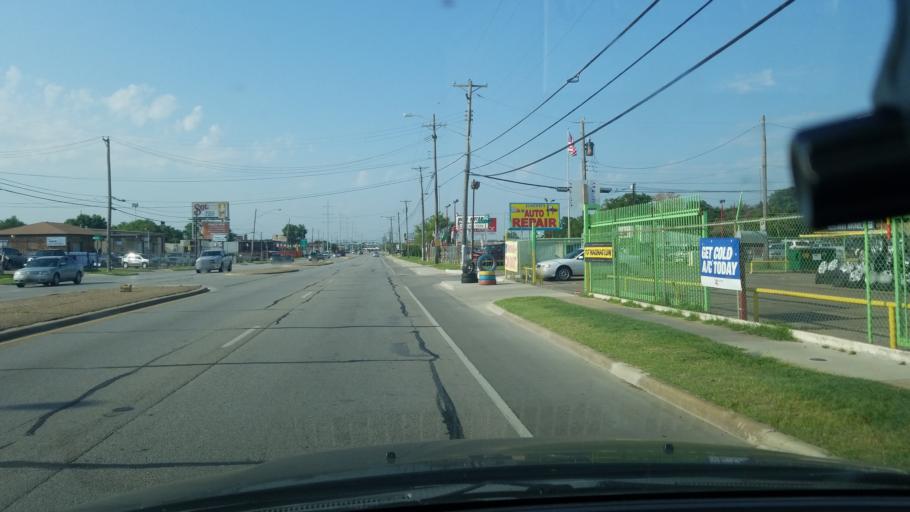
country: US
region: Texas
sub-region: Dallas County
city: Balch Springs
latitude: 32.7231
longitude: -96.6831
